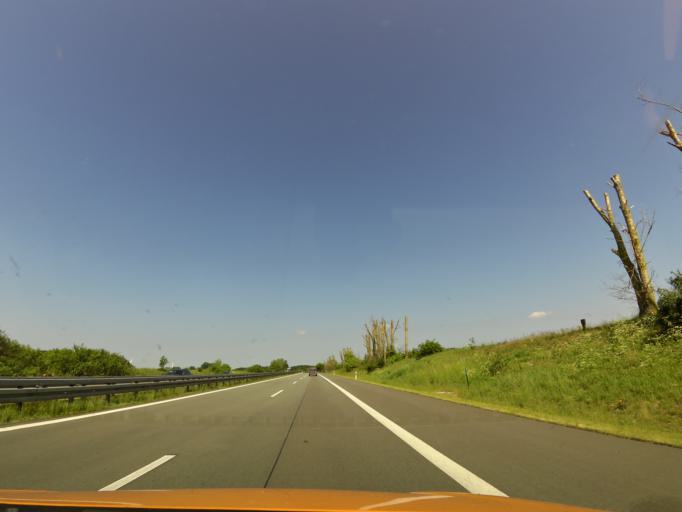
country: DE
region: Brandenburg
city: Gerdshagen
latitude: 53.2488
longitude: 12.1766
